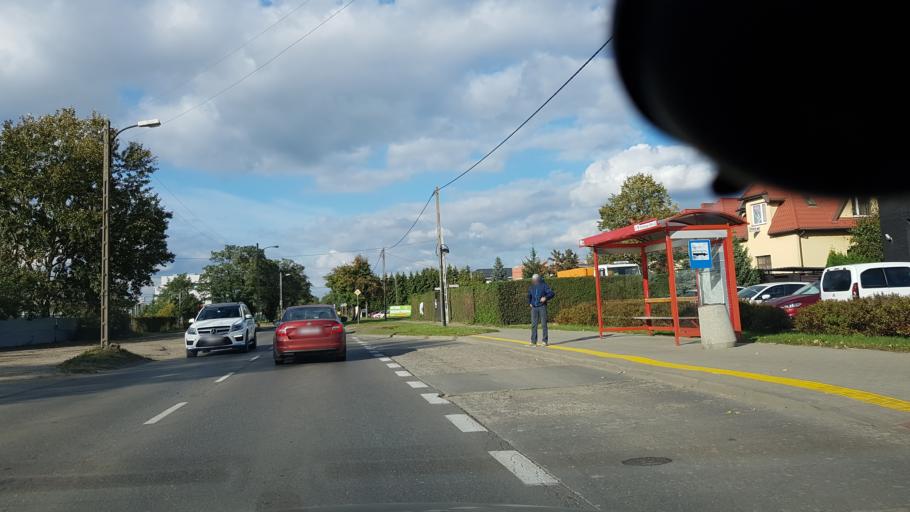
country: PL
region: Masovian Voivodeship
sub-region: Warszawa
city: Targowek
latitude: 52.3073
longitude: 21.0300
